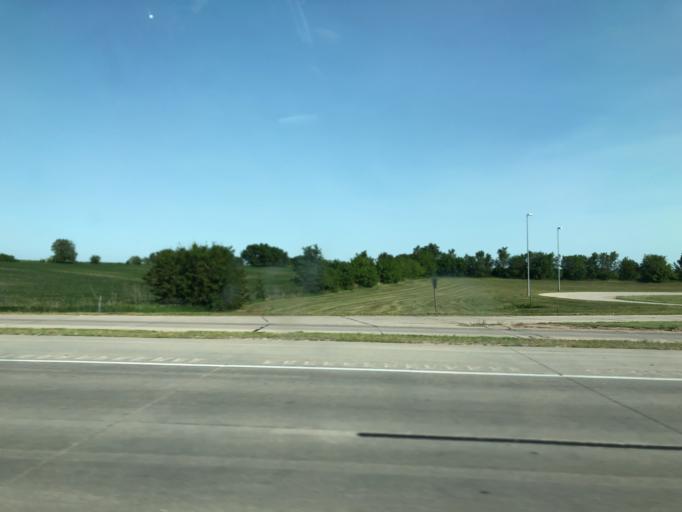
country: US
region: Nebraska
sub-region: Lancaster County
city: Waverly
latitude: 40.9236
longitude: -96.4587
